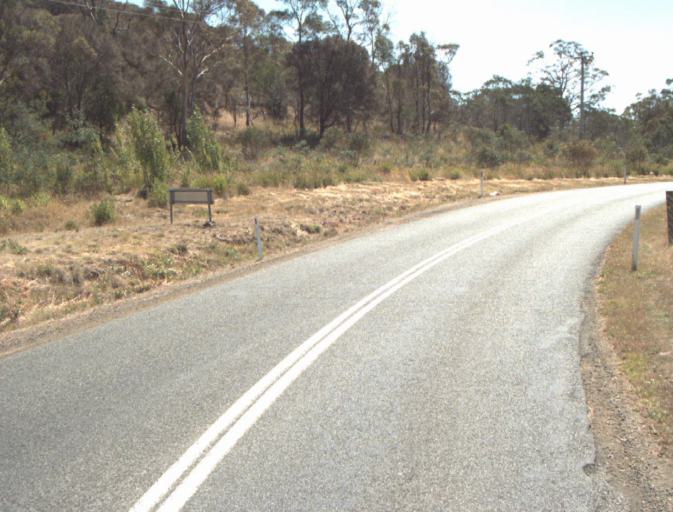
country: AU
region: Tasmania
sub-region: Launceston
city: Mayfield
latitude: -41.3396
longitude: 147.1439
